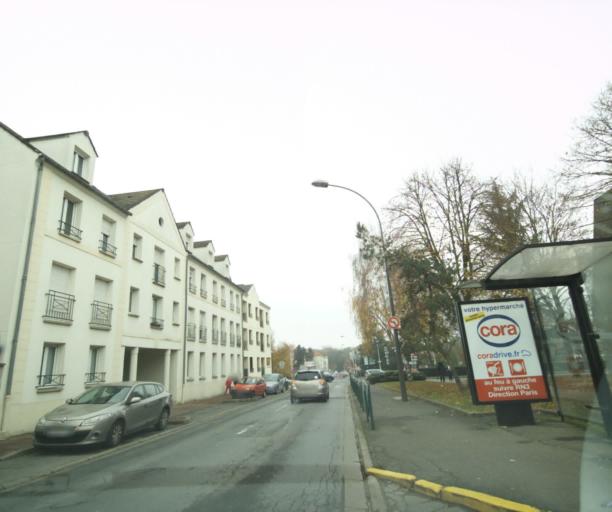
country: FR
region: Ile-de-France
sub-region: Departement de Seine-Saint-Denis
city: Vaujours
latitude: 48.9329
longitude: 2.5672
